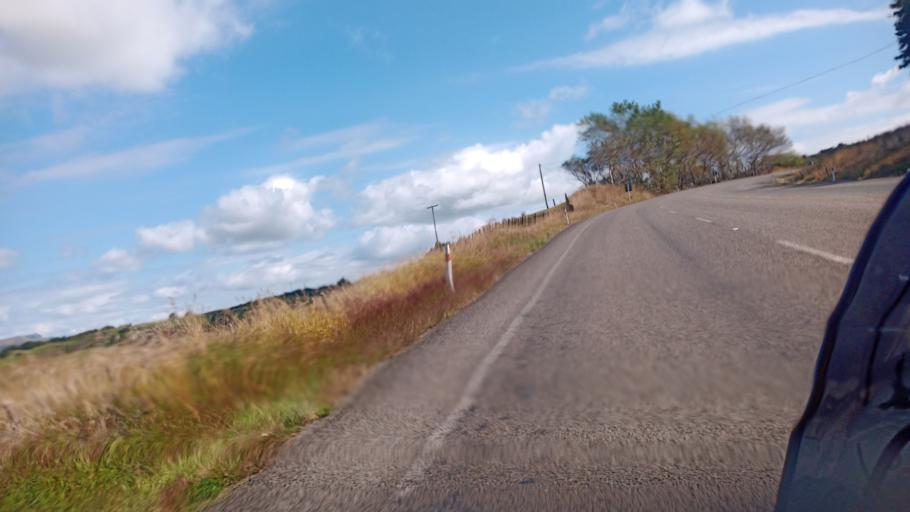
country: NZ
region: Gisborne
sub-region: Gisborne District
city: Gisborne
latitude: -38.5338
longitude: 178.2227
